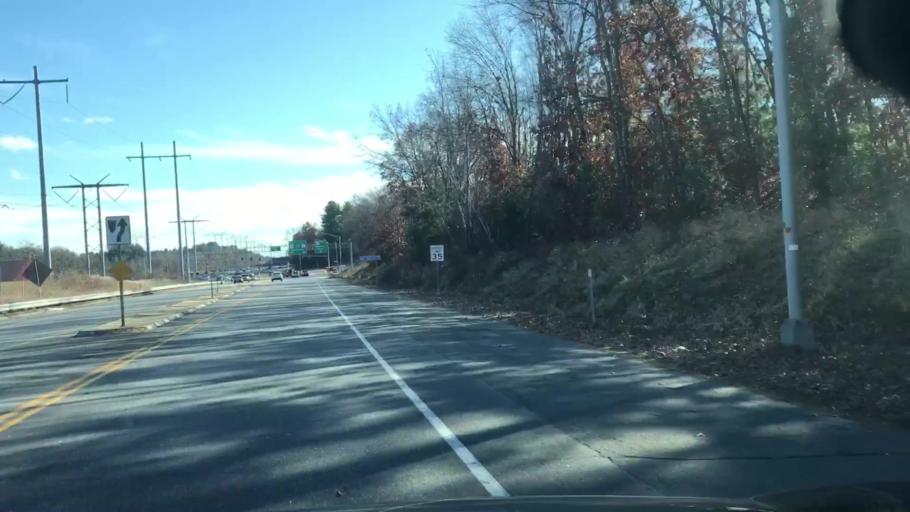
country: US
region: New Hampshire
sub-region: Hillsborough County
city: Bedford
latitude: 42.9623
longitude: -71.5035
